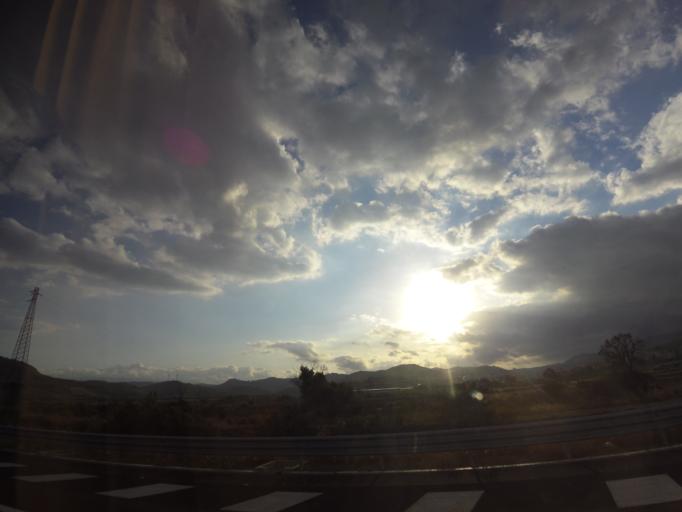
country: IT
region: Calabria
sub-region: Provincia di Catanzaro
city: Catanzaro
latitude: 38.8870
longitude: 16.5563
